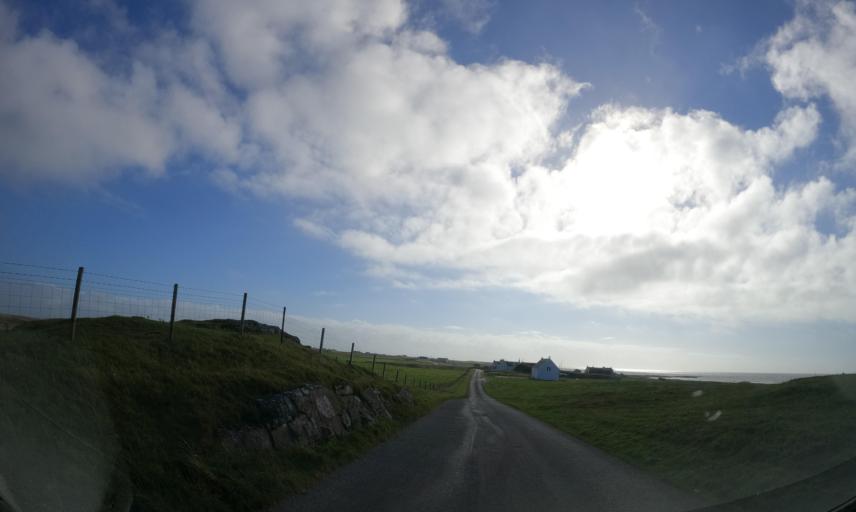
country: GB
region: Scotland
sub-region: Eilean Siar
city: Barra
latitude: 56.4921
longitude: -6.8379
